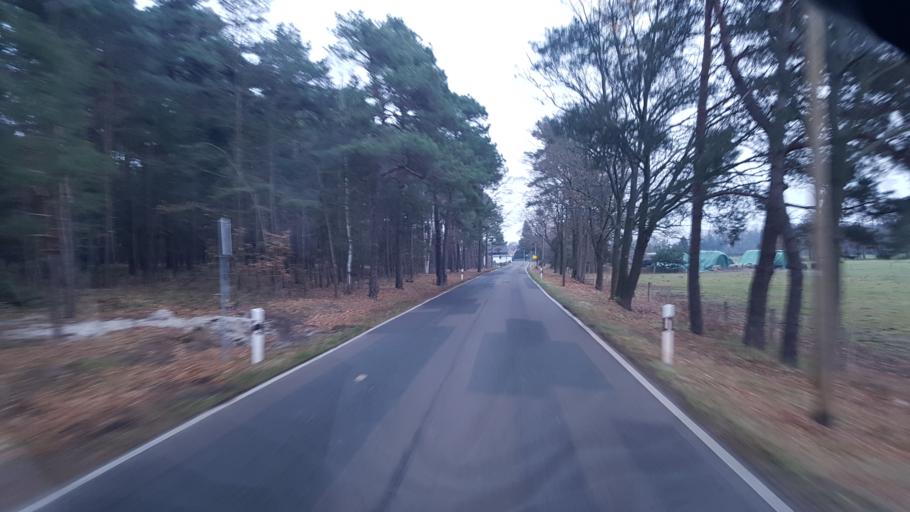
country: DE
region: Brandenburg
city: Briesen
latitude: 51.8517
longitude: 14.2374
